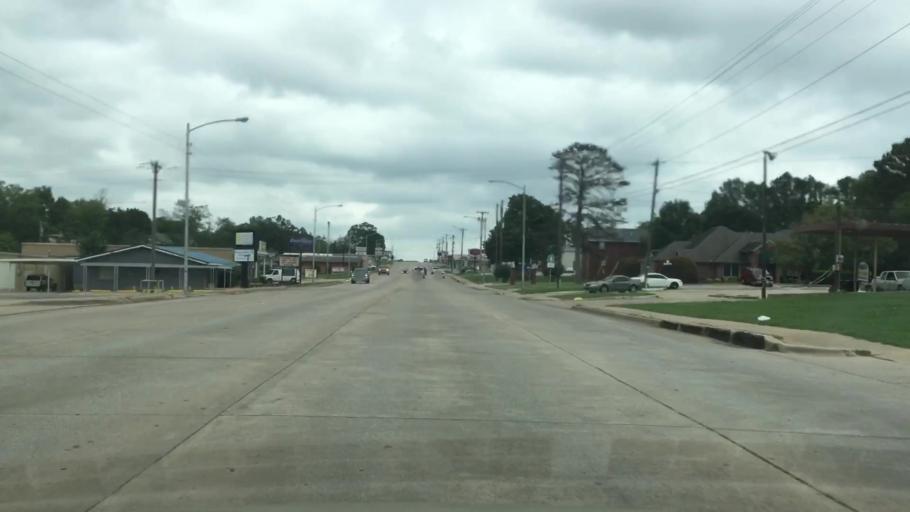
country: US
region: Oklahoma
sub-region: Cherokee County
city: Tahlequah
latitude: 35.9153
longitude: -94.9654
